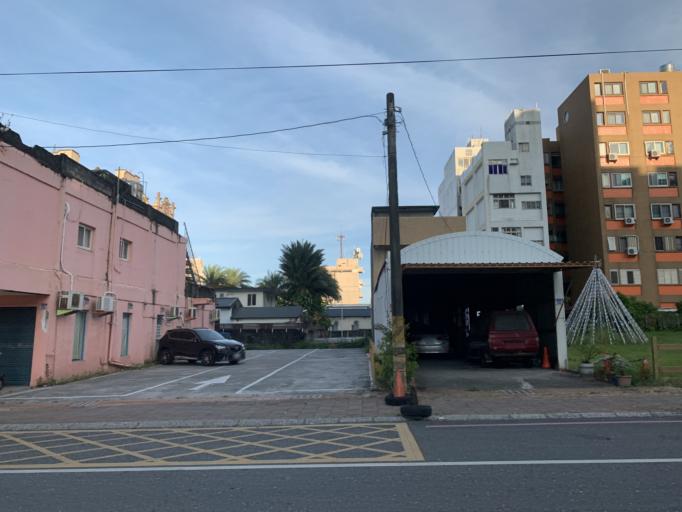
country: TW
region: Taiwan
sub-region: Hualien
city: Hualian
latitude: 23.9927
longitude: 121.6270
